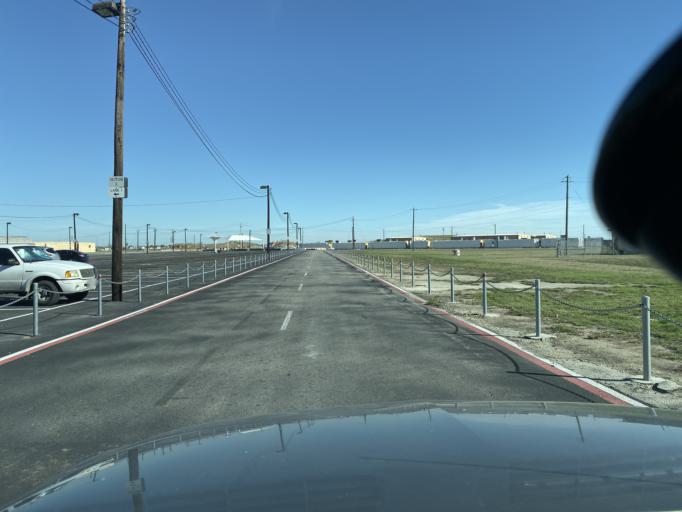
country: US
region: Texas
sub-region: Travis County
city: Hornsby Bend
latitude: 30.1938
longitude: -97.6672
